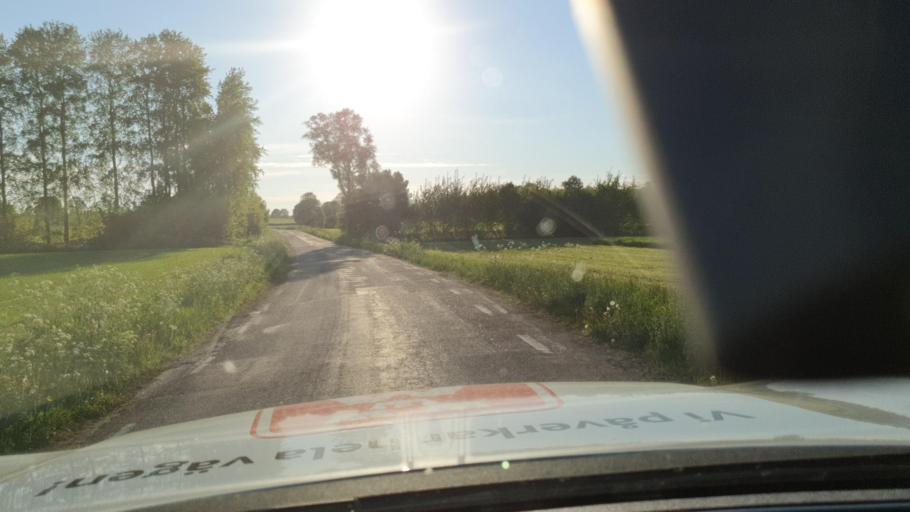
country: SE
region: Vaestra Goetaland
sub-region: Falkopings Kommun
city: Falkoeping
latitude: 58.0787
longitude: 13.5574
